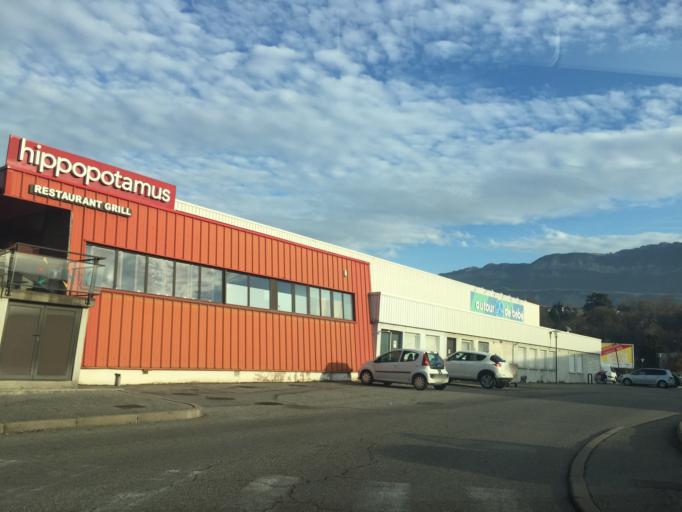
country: FR
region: Rhone-Alpes
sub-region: Departement de la Savoie
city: La Motte-Servolex
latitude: 45.5950
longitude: 5.8969
